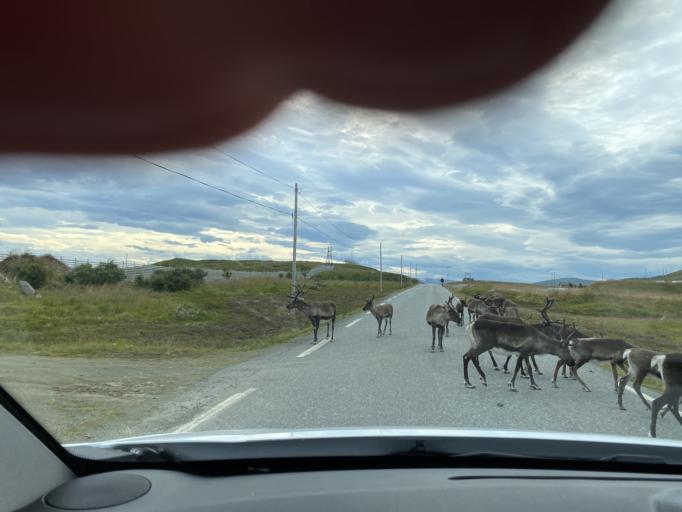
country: NO
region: Troms
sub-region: Karlsoy
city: Hansnes
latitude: 70.1007
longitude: 20.1072
